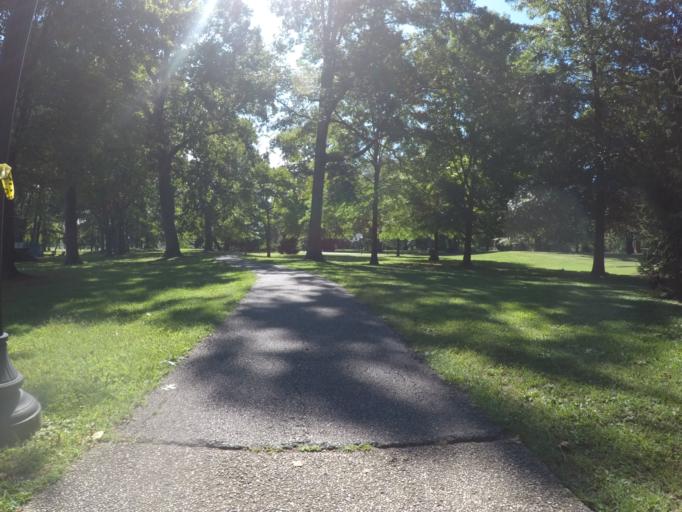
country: US
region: Kentucky
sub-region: Boyd County
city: Ashland
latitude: 38.4749
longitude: -82.6388
